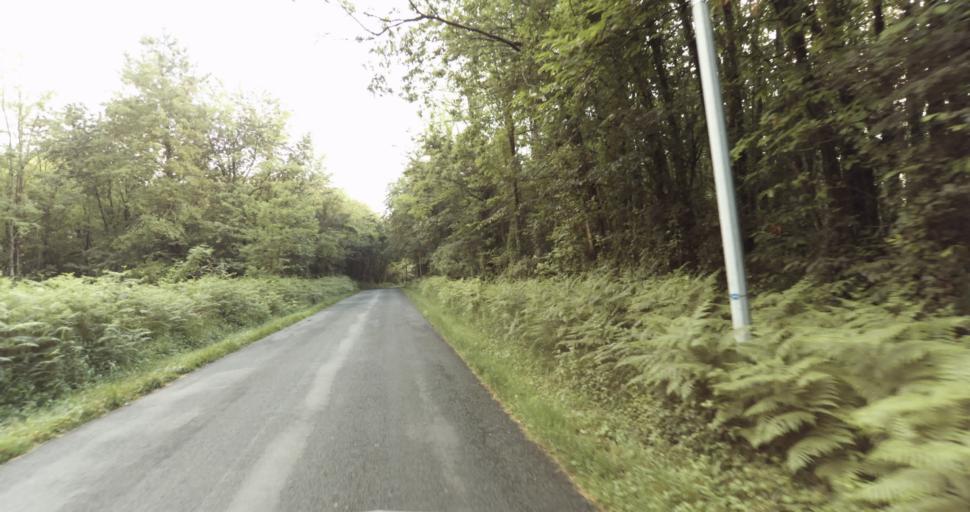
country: FR
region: Aquitaine
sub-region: Departement de la Dordogne
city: Le Bugue
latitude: 44.9343
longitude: 0.8179
